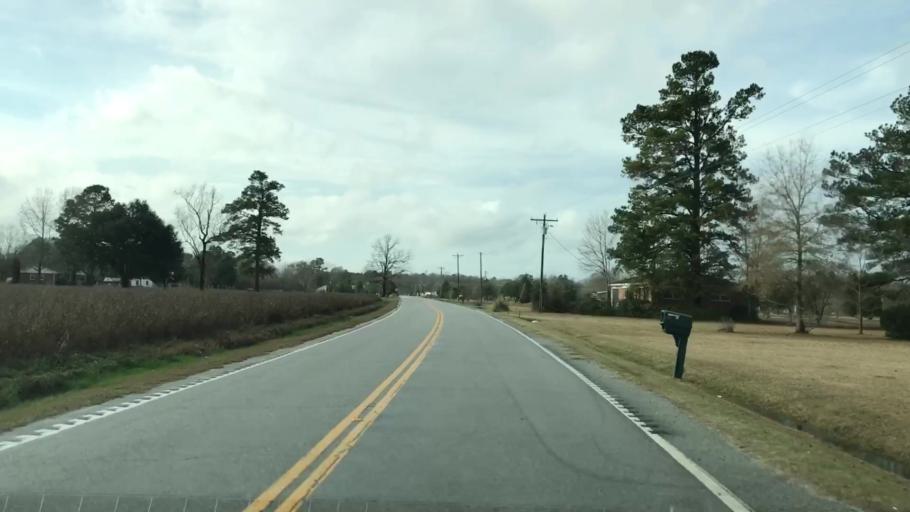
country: US
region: South Carolina
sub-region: Williamsburg County
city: Andrews
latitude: 33.5017
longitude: -79.5183
